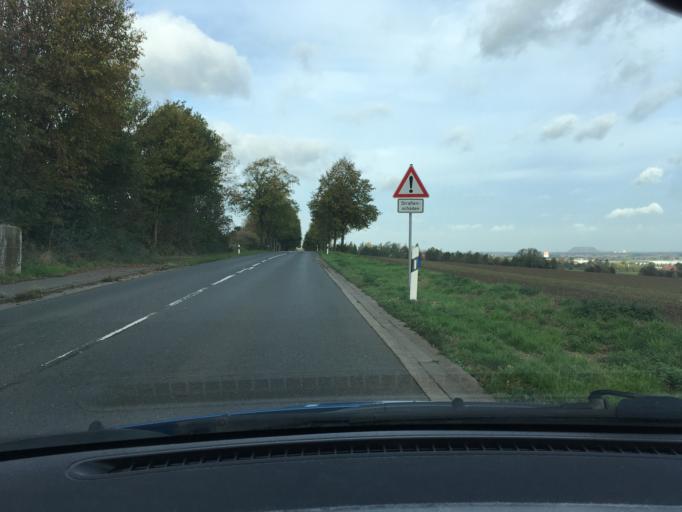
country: DE
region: Lower Saxony
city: Barsinghausen
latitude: 52.3209
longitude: 9.4271
